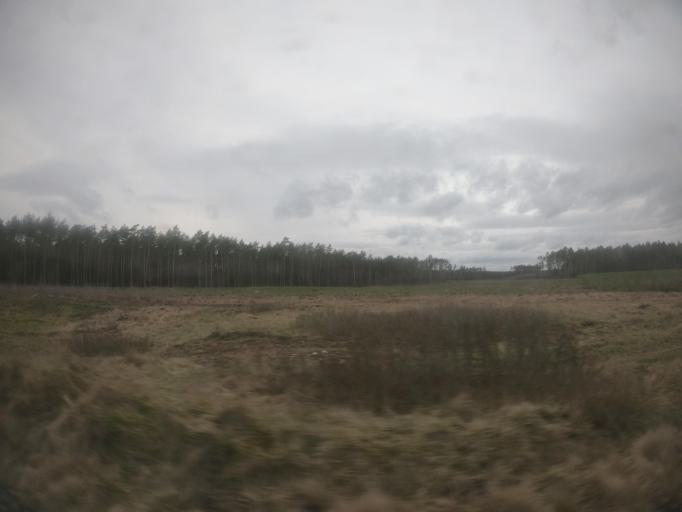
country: PL
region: Pomeranian Voivodeship
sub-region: Powiat czluchowski
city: Czarne
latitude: 53.7676
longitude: 16.8550
